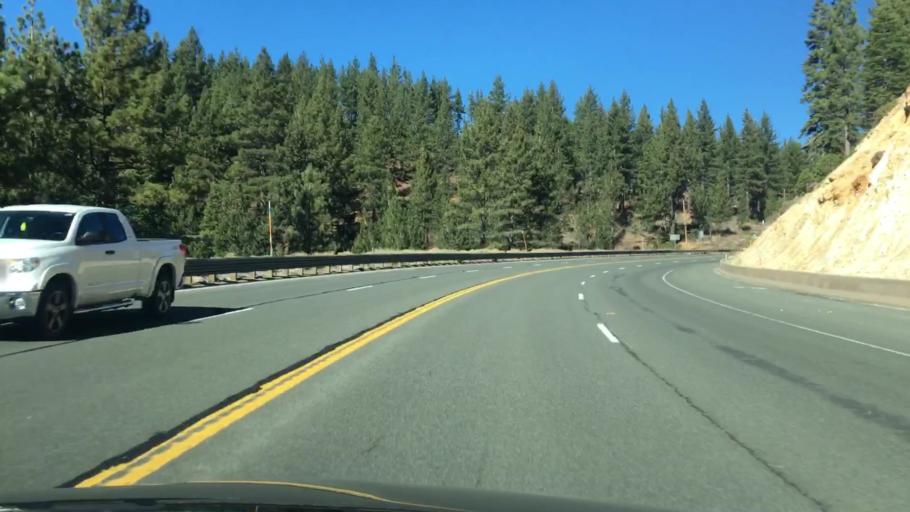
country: US
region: Nevada
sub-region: Douglas County
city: Kingsbury
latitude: 39.0945
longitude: -119.9106
